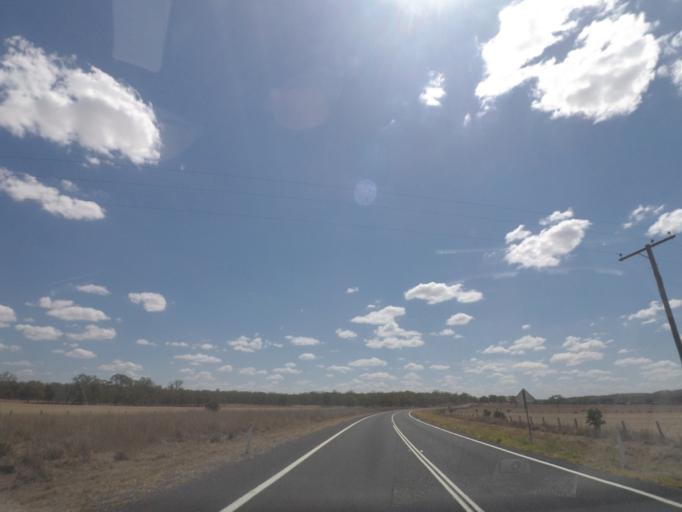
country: AU
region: Queensland
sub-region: Southern Downs
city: Warwick
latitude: -28.1837
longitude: 151.8148
